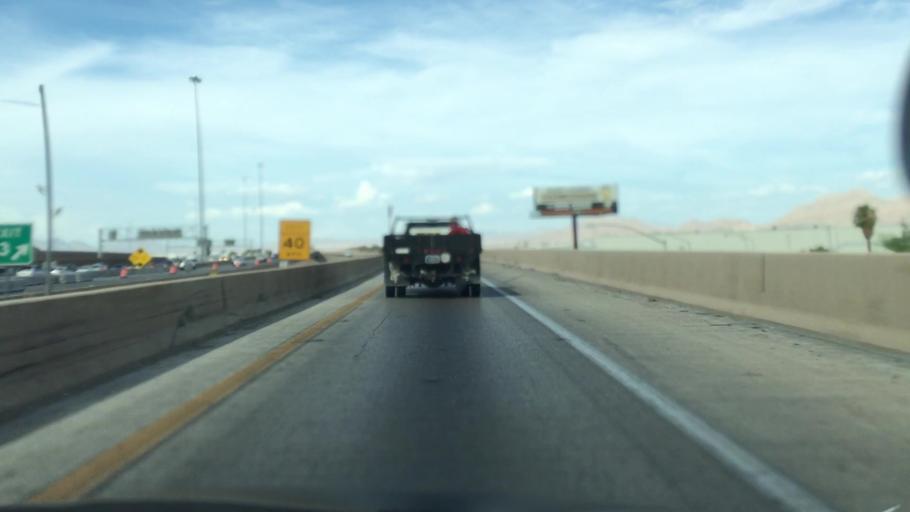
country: US
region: Nevada
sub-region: Clark County
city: Las Vegas
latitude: 36.1781
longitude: -115.1490
